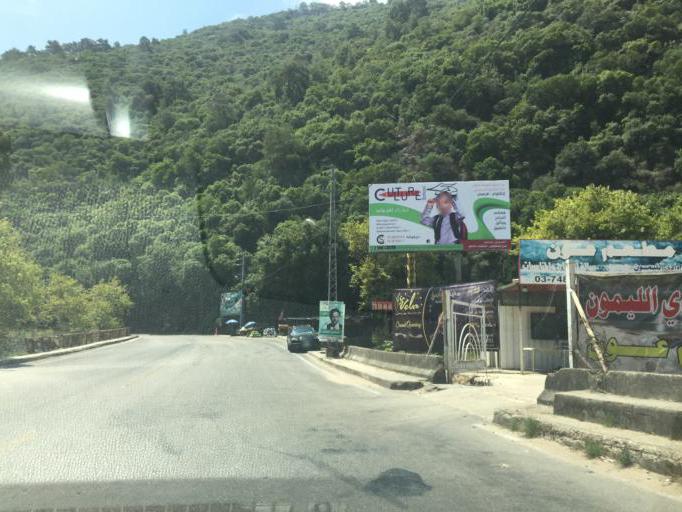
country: LB
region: Mont-Liban
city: Beit ed Dine
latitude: 33.7015
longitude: 35.4684
